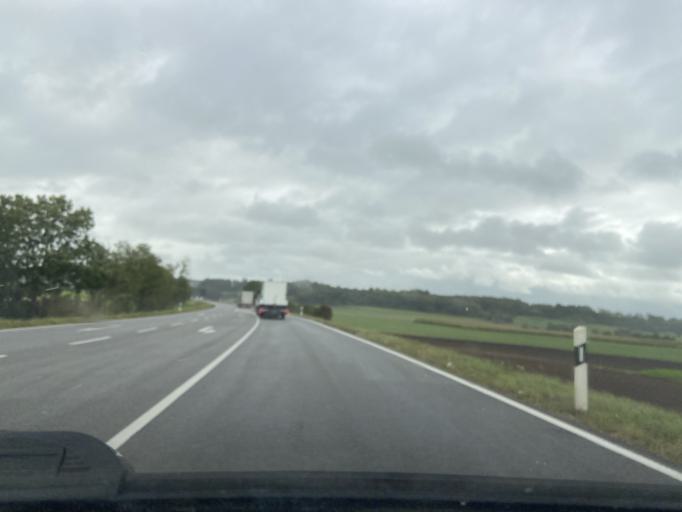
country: DE
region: Baden-Wuerttemberg
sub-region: Tuebingen Region
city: Messkirch
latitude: 48.0011
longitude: 9.1752
